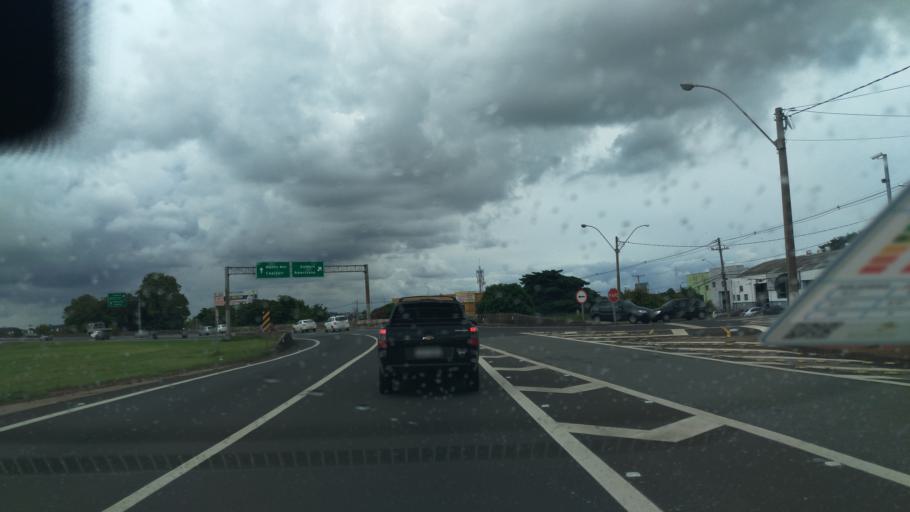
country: BR
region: Sao Paulo
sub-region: Campinas
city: Campinas
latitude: -22.8970
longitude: -47.1077
